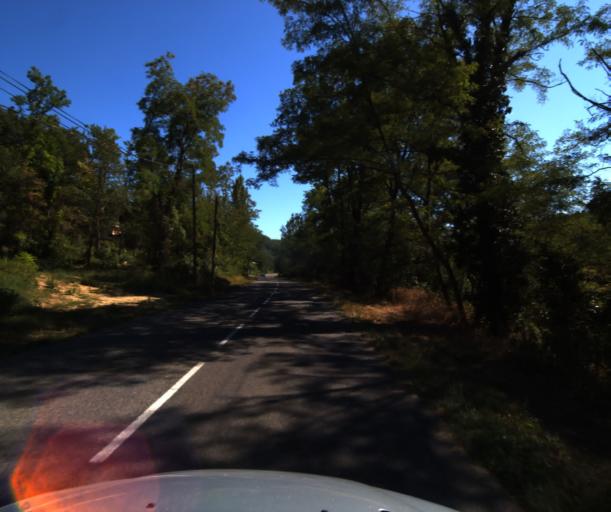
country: FR
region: Midi-Pyrenees
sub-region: Departement de la Haute-Garonne
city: Eaunes
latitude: 43.4367
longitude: 1.3267
